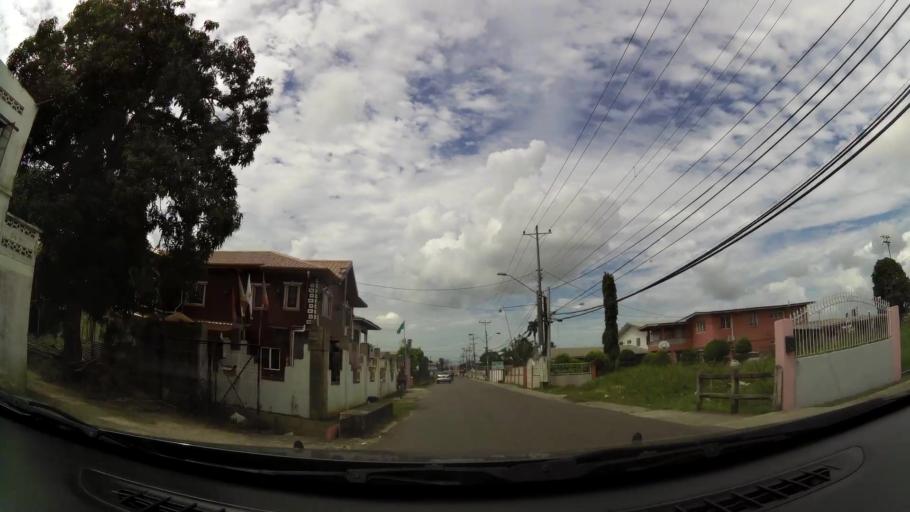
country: TT
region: Couva-Tabaquite-Talparo
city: Couva
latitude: 10.4037
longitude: -61.4686
